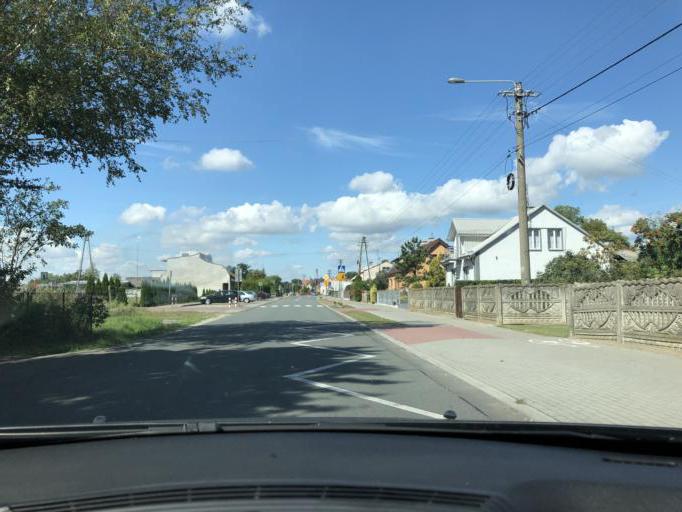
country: PL
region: Lodz Voivodeship
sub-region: Powiat wieruszowski
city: Czastary
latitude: 51.2411
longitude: 18.3280
